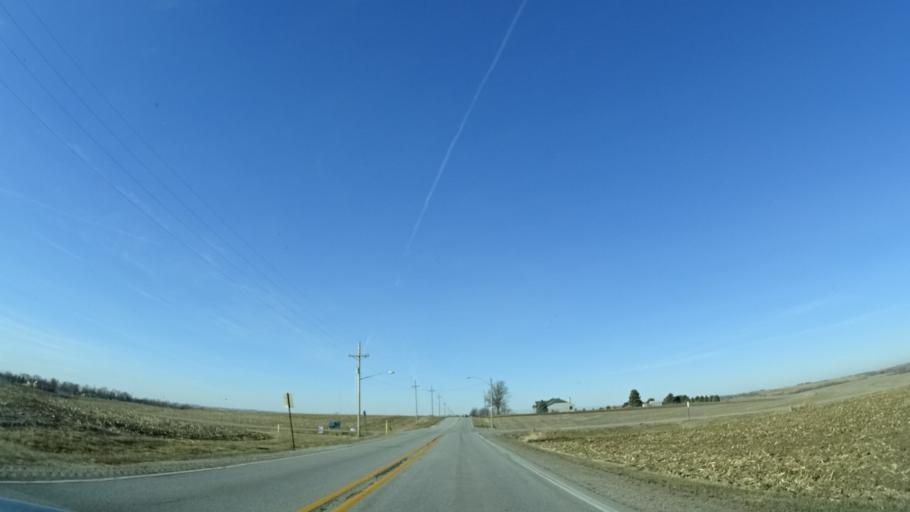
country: US
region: Nebraska
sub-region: Sarpy County
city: Springfield
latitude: 41.0890
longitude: -96.1184
